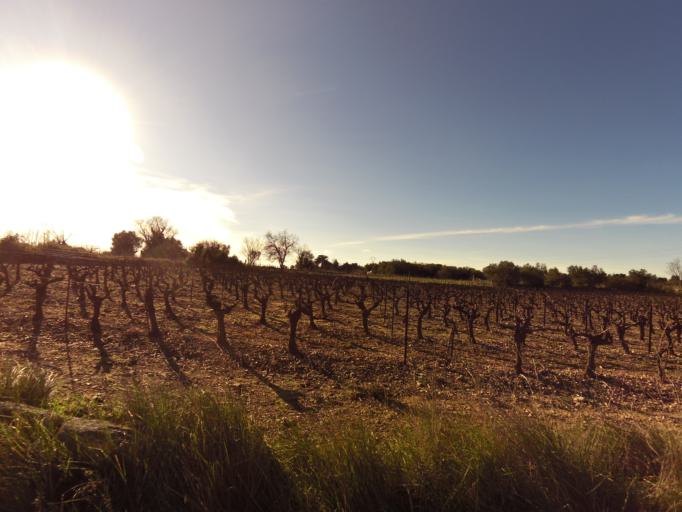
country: FR
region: Languedoc-Roussillon
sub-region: Departement du Gard
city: Aigues-Vives
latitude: 43.7456
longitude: 4.1776
